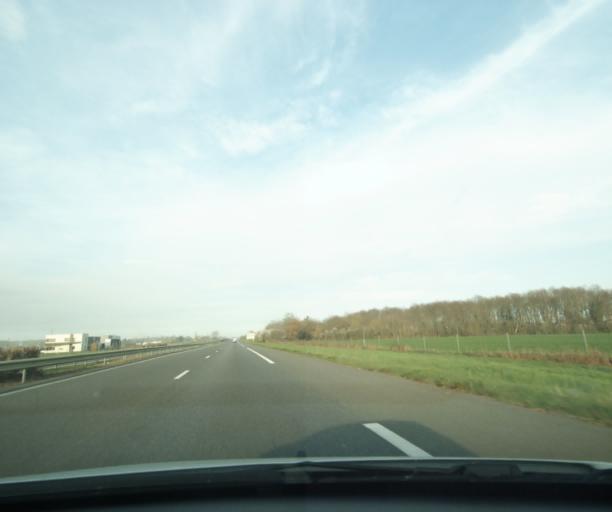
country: FR
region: Midi-Pyrenees
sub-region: Departement de la Haute-Garonne
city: Le Fousseret
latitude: 43.2667
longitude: 1.1263
